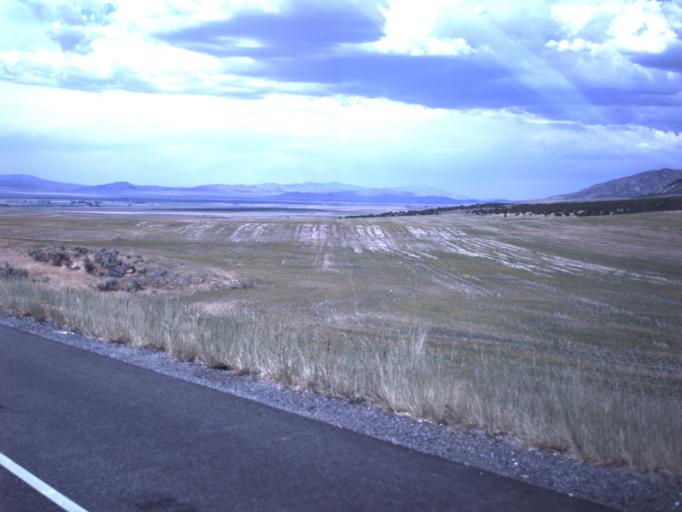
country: US
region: Idaho
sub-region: Oneida County
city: Malad City
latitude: 41.9364
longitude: -112.6554
